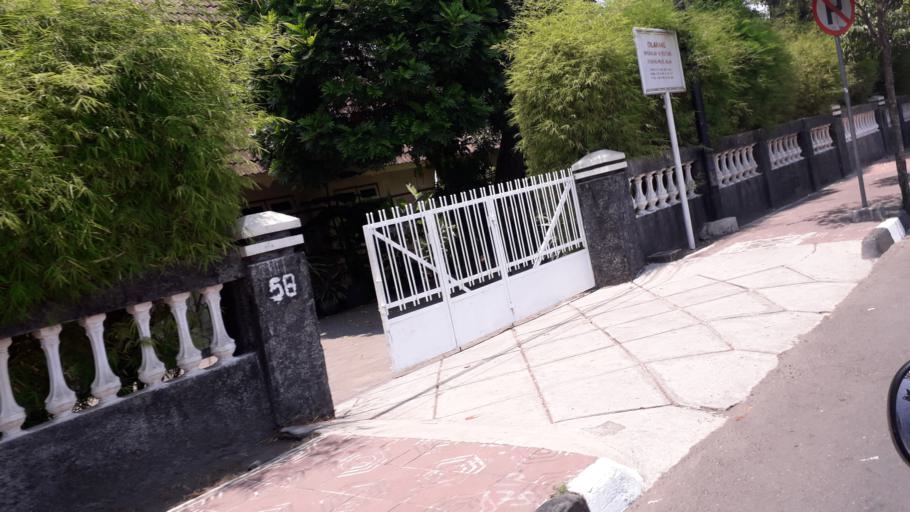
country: ID
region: Daerah Istimewa Yogyakarta
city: Yogyakarta
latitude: -7.7758
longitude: 110.3680
